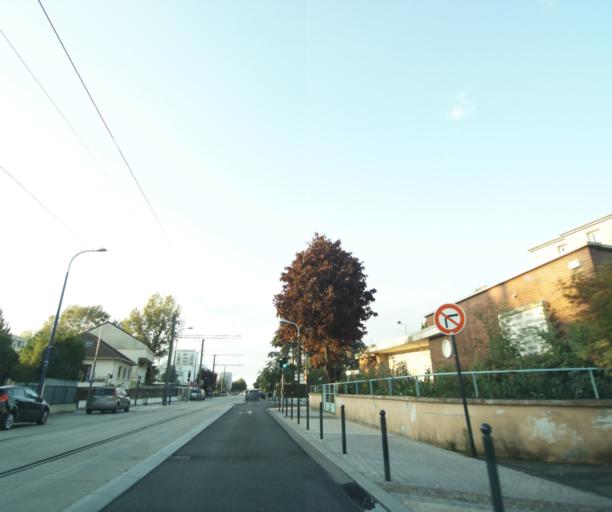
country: FR
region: Ile-de-France
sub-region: Departement des Hauts-de-Seine
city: Meudon
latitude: 48.7831
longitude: 2.2385
